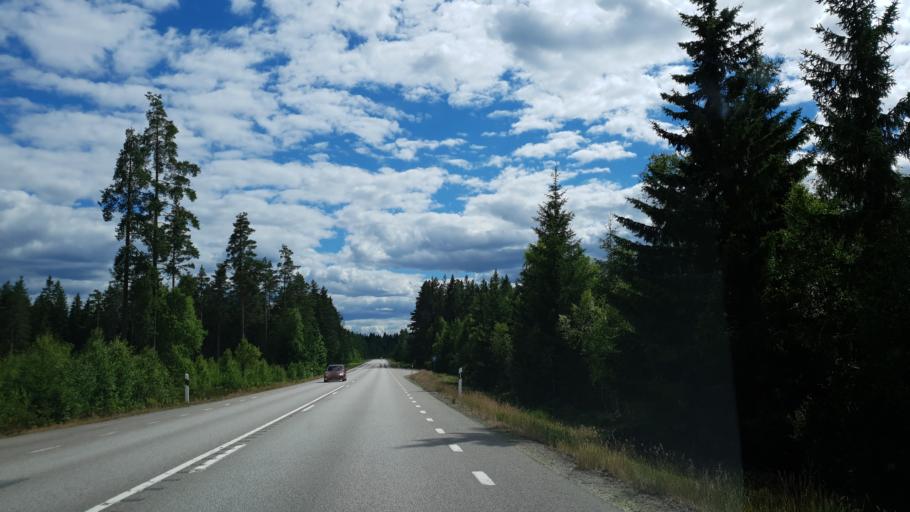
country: SE
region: Kronoberg
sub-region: Uppvidinge Kommun
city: Lenhovda
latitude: 56.9066
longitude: 15.3676
